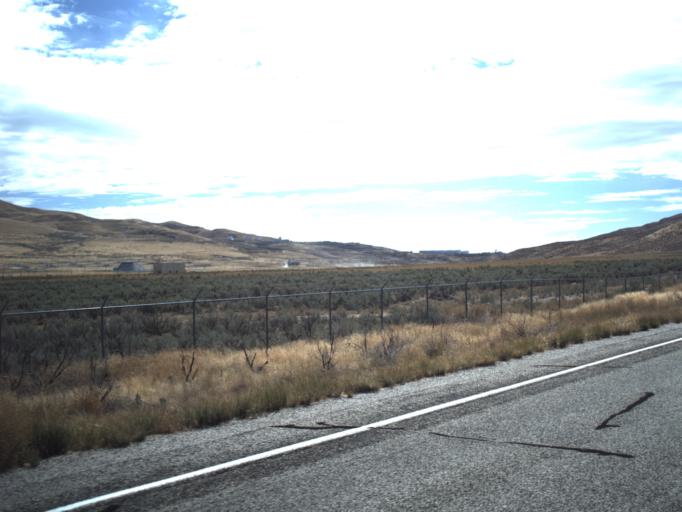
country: US
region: Utah
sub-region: Box Elder County
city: Tremonton
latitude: 41.7171
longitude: -112.4519
